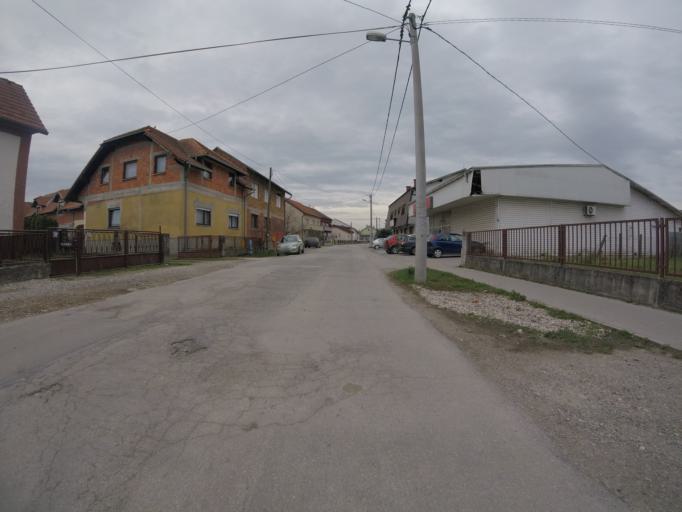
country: HR
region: Grad Zagreb
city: Odra
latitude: 45.7139
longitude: 16.0228
